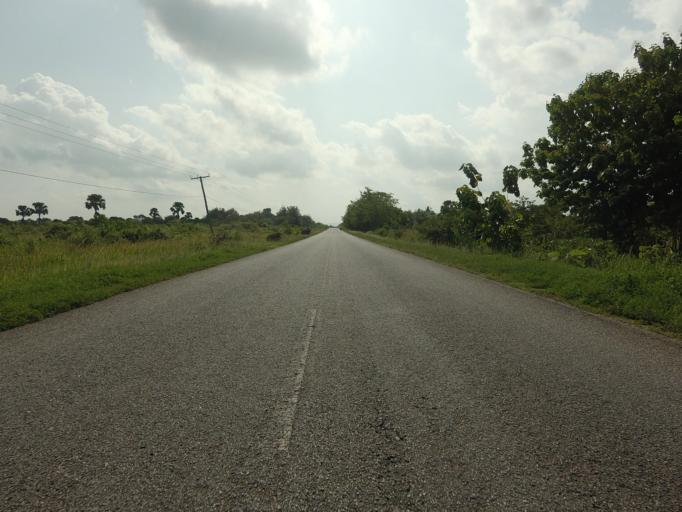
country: GH
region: Volta
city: Ho
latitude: 6.5789
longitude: 0.5821
